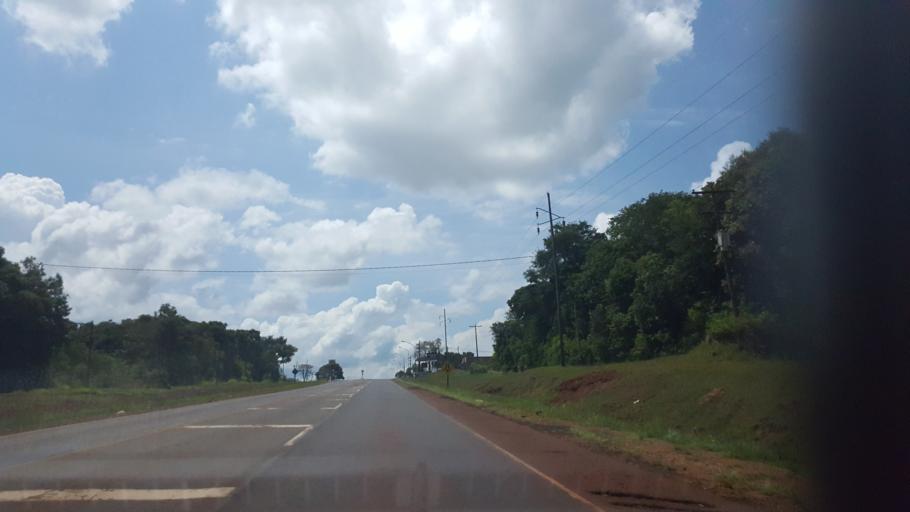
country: AR
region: Misiones
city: Puerto Rico
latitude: -26.8262
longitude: -55.0306
